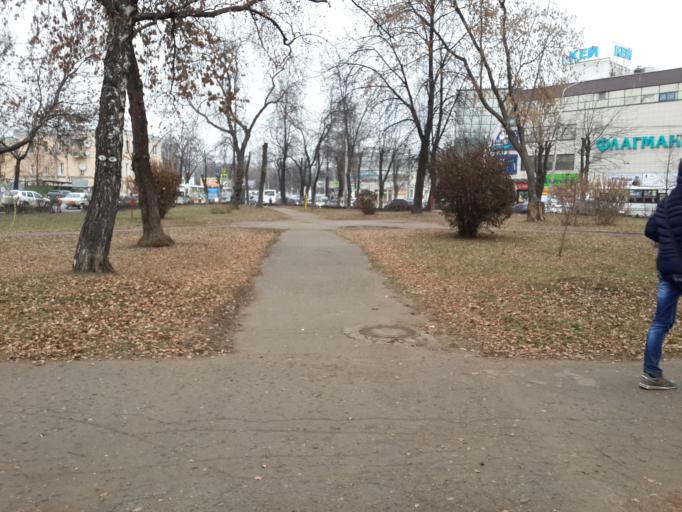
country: RU
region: Jaroslavl
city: Yaroslavl
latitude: 57.6370
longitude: 39.8812
